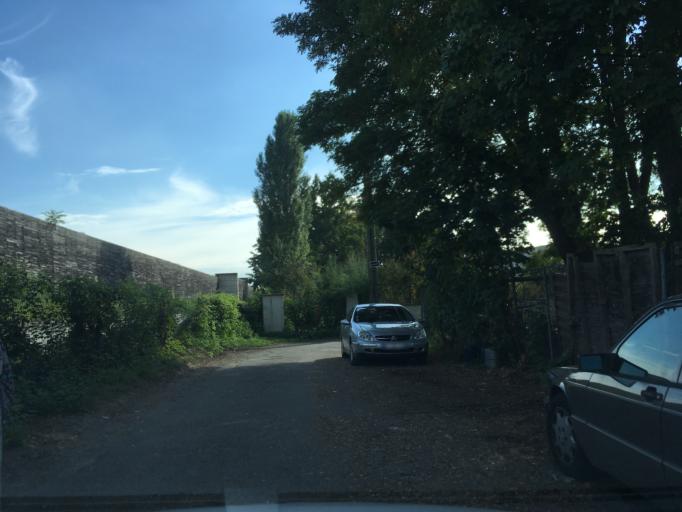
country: FR
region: Alsace
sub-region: Departement du Haut-Rhin
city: Horbourg-Wihr
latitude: 48.0777
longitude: 7.3846
